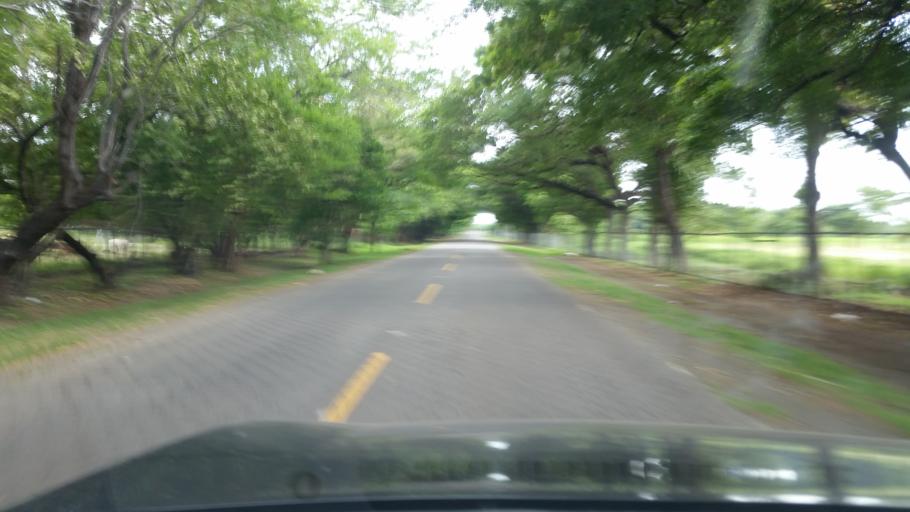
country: NI
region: Managua
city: Carlos Fonseca Amador
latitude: 12.0680
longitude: -86.5013
